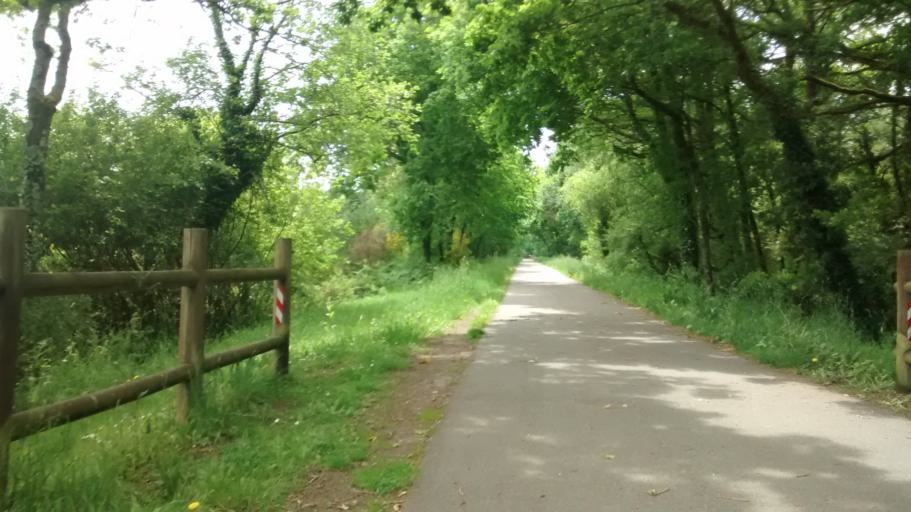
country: FR
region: Brittany
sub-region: Departement du Morbihan
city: Questembert
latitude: 47.6900
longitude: -2.4381
